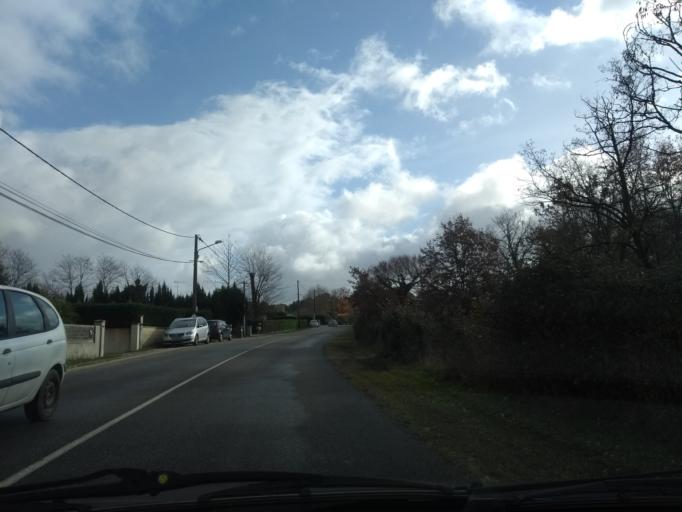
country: FR
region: Aquitaine
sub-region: Departement de la Gironde
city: Belin-Beliet
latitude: 44.4920
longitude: -0.7841
